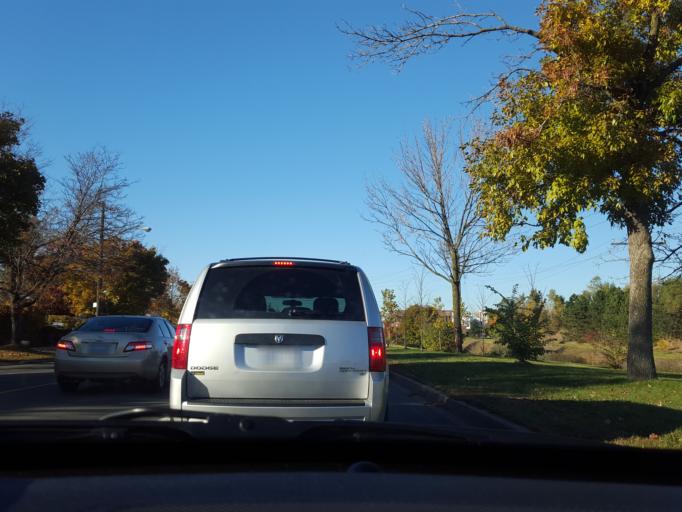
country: CA
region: Ontario
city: Scarborough
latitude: 43.7949
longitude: -79.2717
